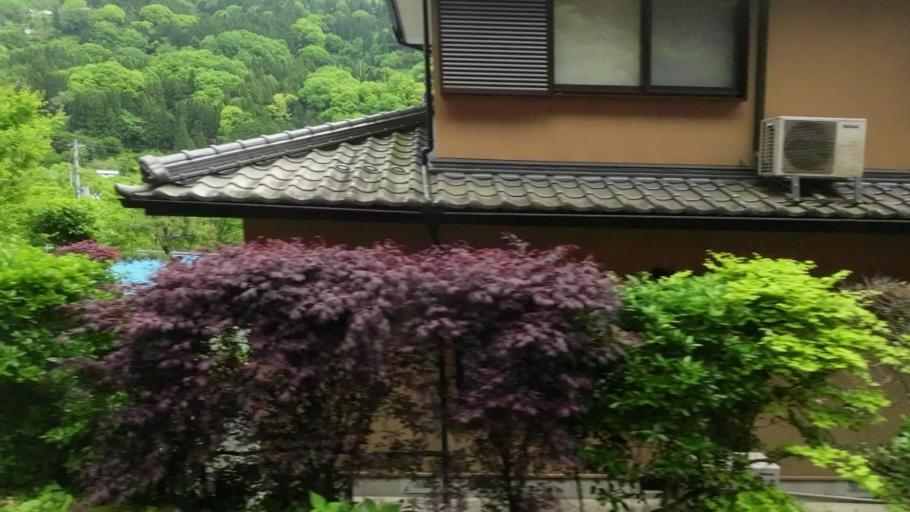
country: JP
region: Tokushima
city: Ikedacho
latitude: 33.9741
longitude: 133.7819
